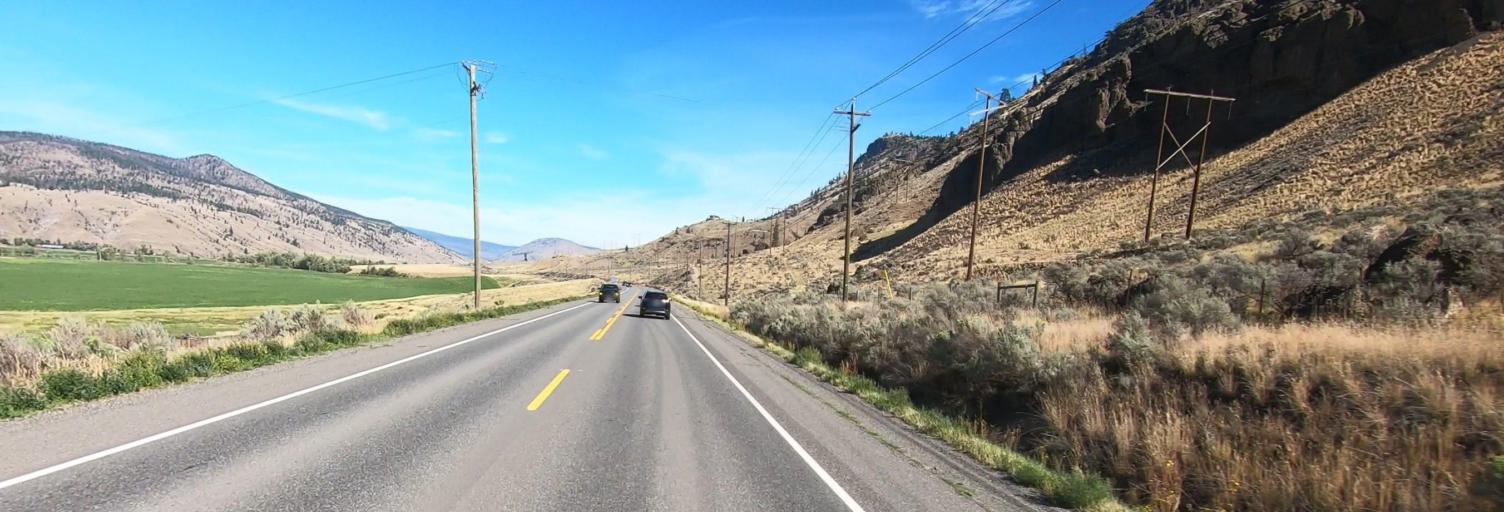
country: CA
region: British Columbia
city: Cache Creek
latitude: 50.8725
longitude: -121.3919
